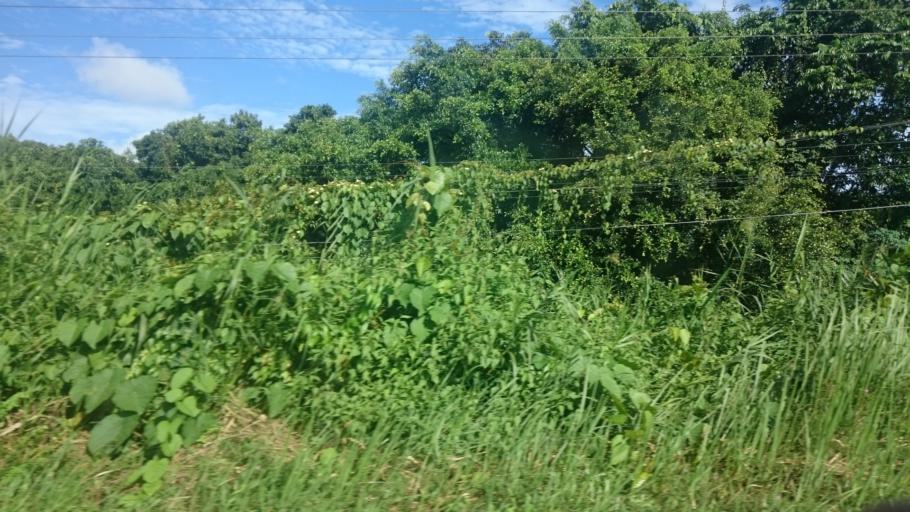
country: MY
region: Sarawak
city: Limbang
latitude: 4.6690
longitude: 114.9832
